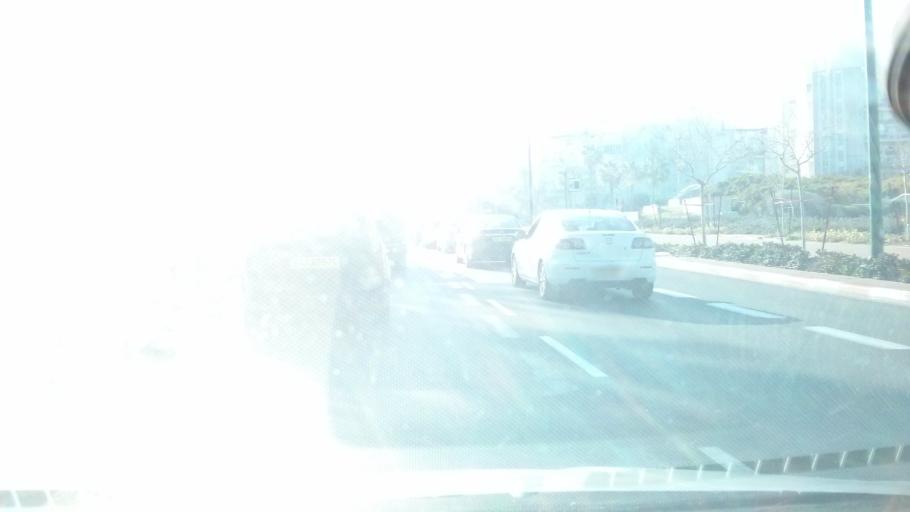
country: IL
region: Central District
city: Even Yehuda
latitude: 32.2791
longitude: 34.8488
